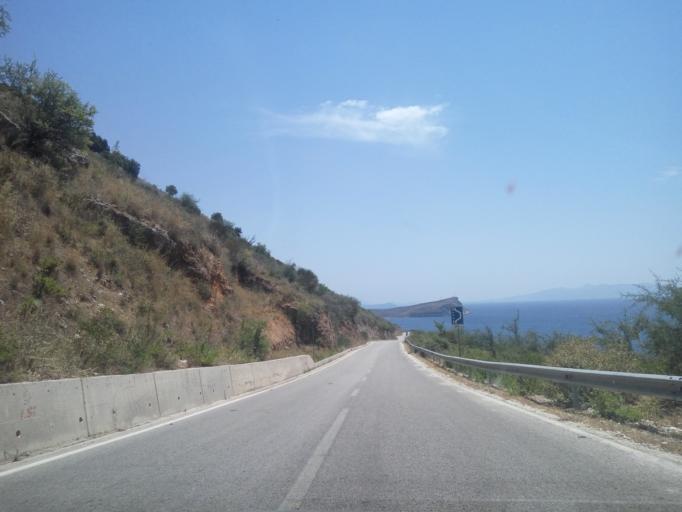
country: AL
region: Vlore
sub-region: Rrethi i Vlores
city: Himare
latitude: 40.0780
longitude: 19.7770
